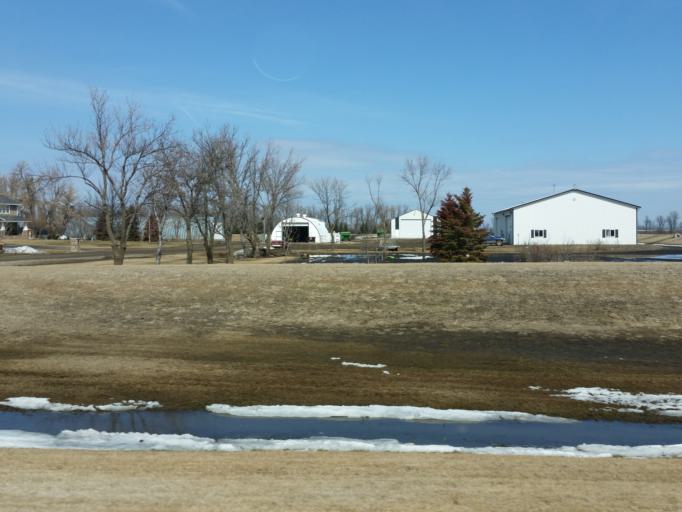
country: US
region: North Dakota
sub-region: Walsh County
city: Grafton
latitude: 48.2955
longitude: -97.2409
